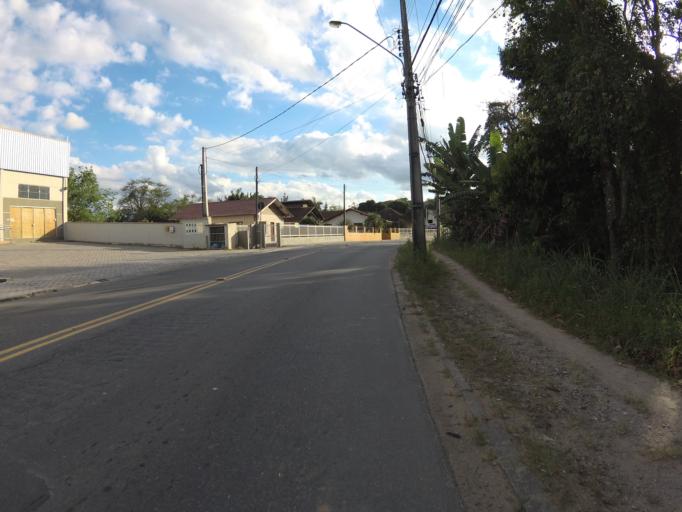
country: BR
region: Santa Catarina
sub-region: Blumenau
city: Blumenau
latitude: -26.8751
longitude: -49.0979
